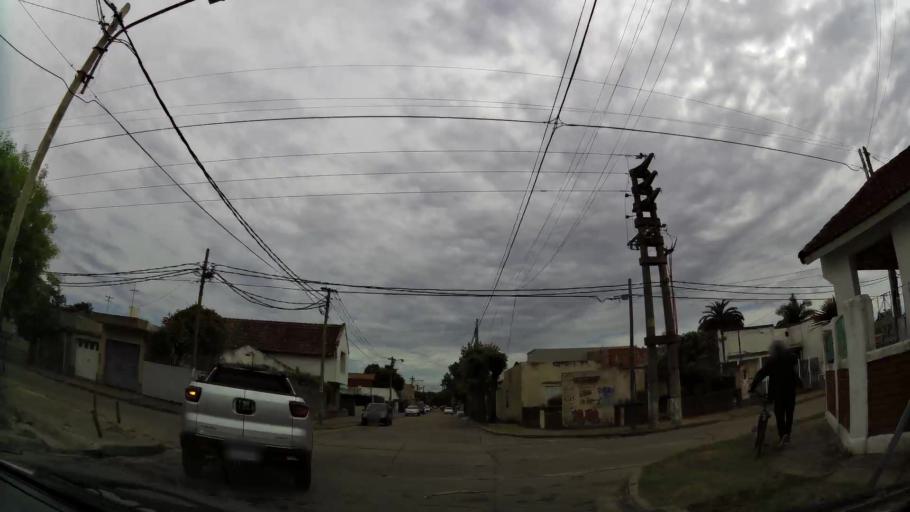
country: AR
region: Buenos Aires
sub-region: Partido de Quilmes
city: Quilmes
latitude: -34.7517
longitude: -58.2117
